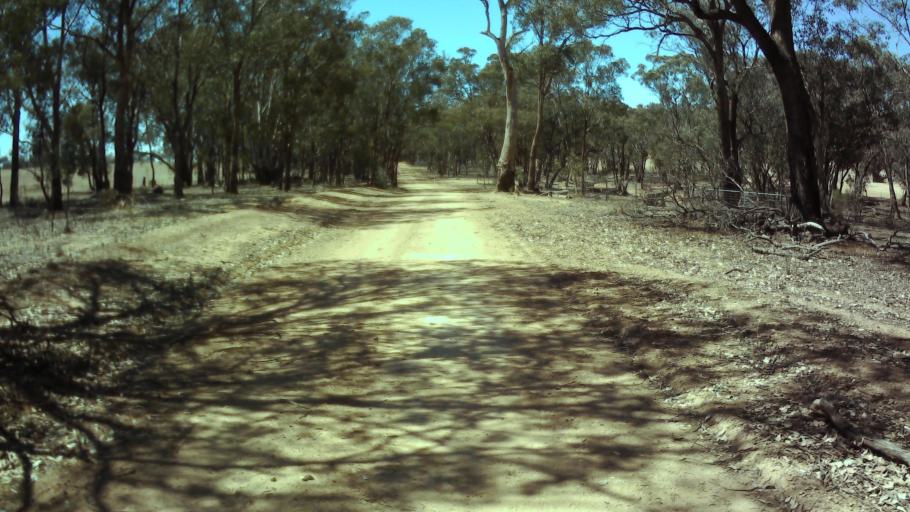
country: AU
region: New South Wales
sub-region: Weddin
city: Grenfell
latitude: -33.9591
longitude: 148.0864
